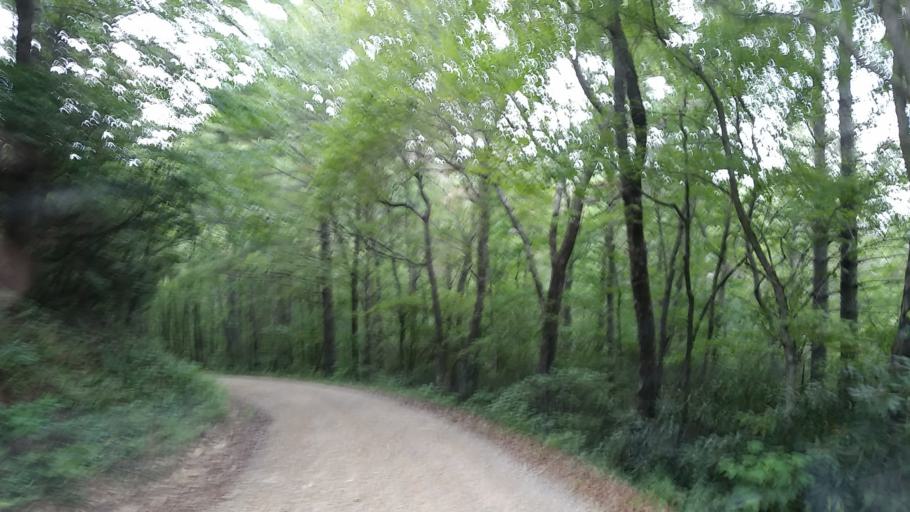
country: US
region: Georgia
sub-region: Lumpkin County
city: Dahlonega
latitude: 34.6516
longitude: -84.0656
